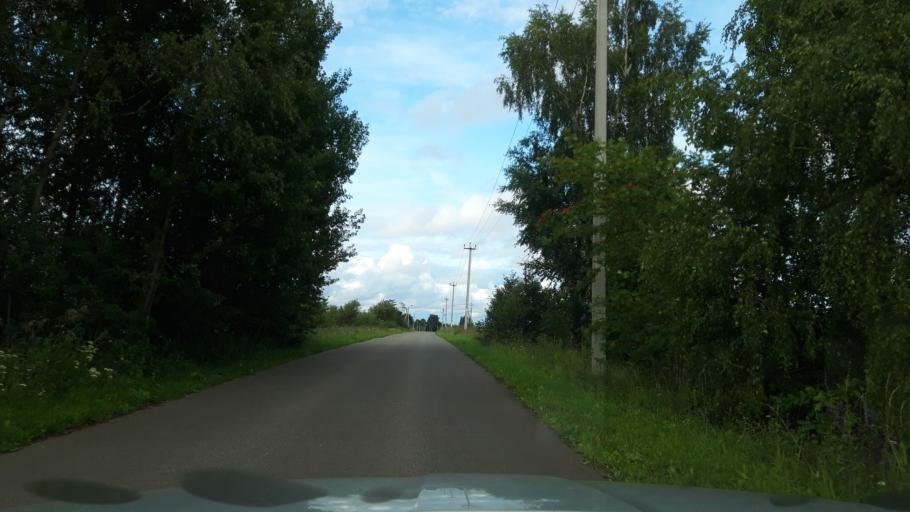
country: RU
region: Moskovskaya
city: Istra
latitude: 56.1002
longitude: 36.8029
